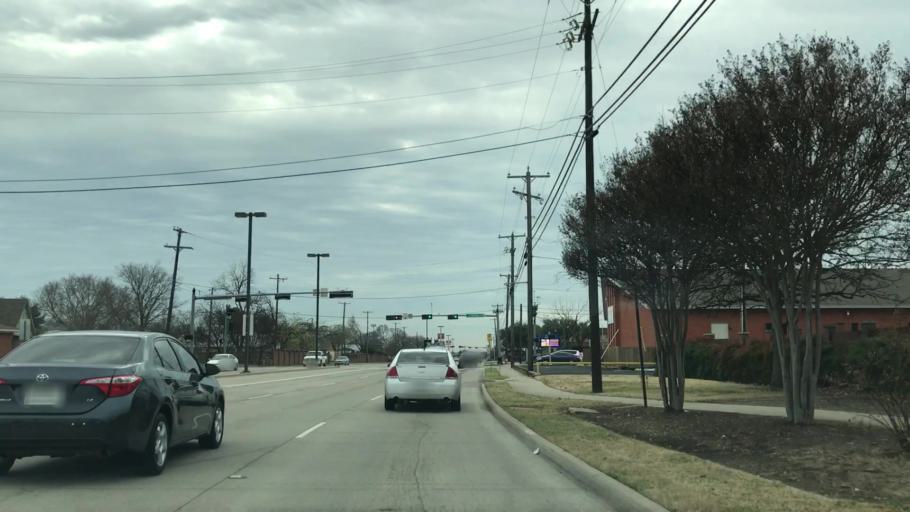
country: US
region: Texas
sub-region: Dallas County
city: Carrollton
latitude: 32.9499
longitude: -96.8904
